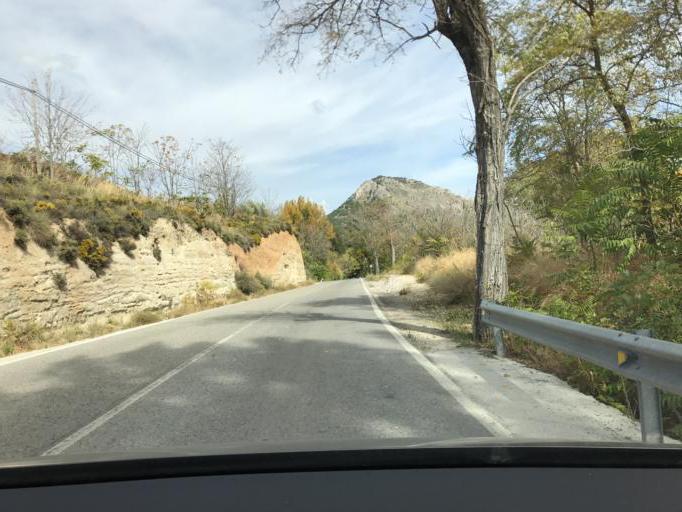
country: ES
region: Andalusia
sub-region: Provincia de Granada
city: Huetor Santillan
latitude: 37.2286
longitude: -3.5024
